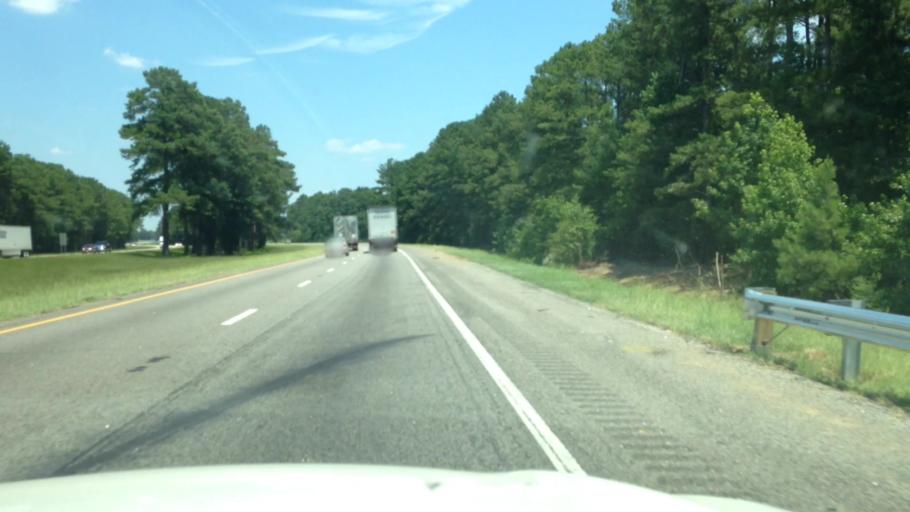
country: US
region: South Carolina
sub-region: Dillon County
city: Dillon
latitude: 34.4105
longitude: -79.4237
